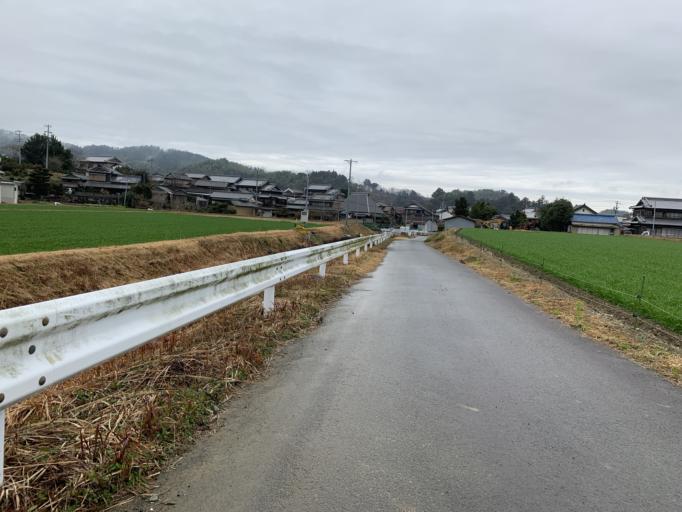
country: JP
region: Mie
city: Ise
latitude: 34.4765
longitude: 136.5464
